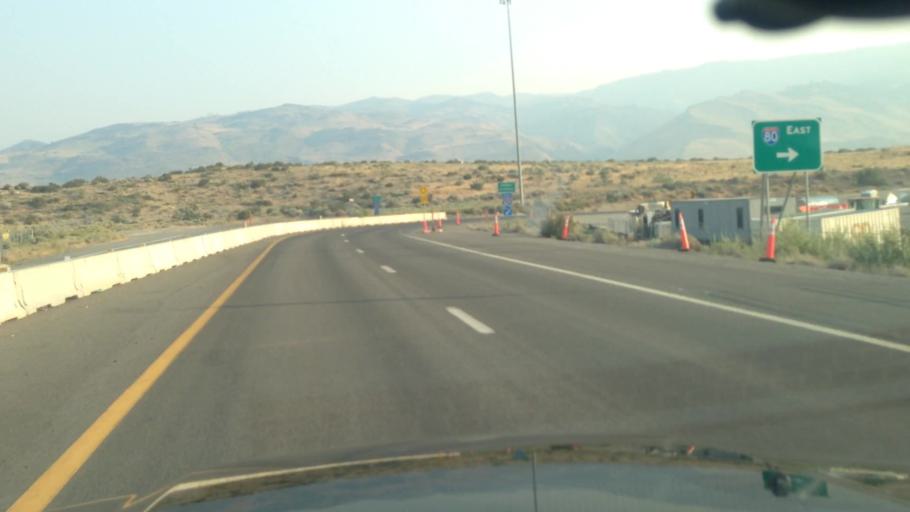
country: US
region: Nevada
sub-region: Washoe County
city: Mogul
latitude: 39.5153
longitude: -119.8872
